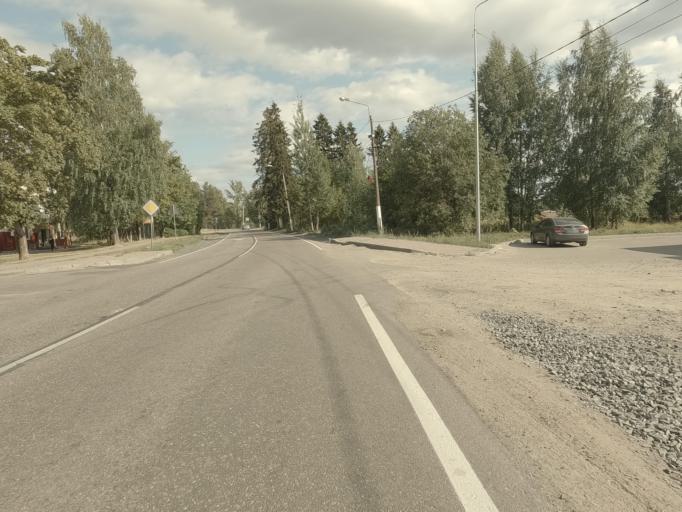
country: RU
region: Leningrad
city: Kamennogorsk
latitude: 60.9485
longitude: 29.1318
